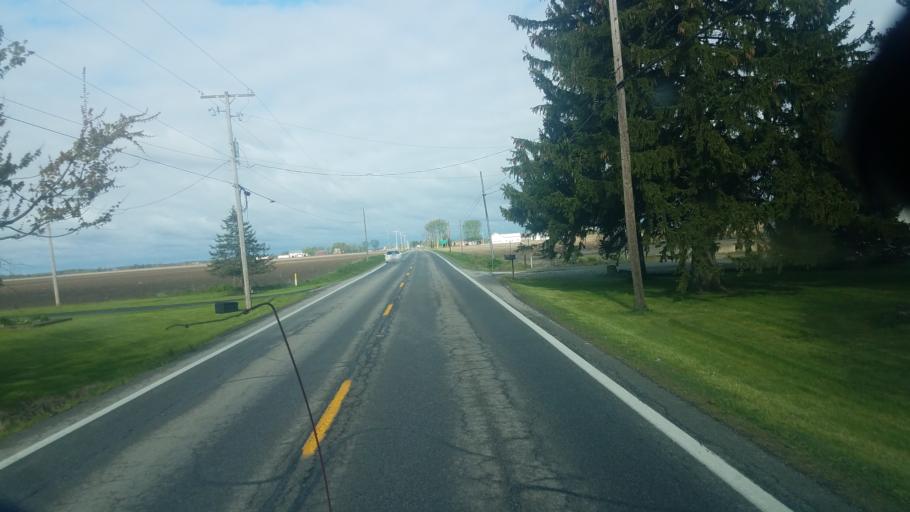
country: US
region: Ohio
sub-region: Marion County
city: Marion
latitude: 40.5828
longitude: -83.0001
